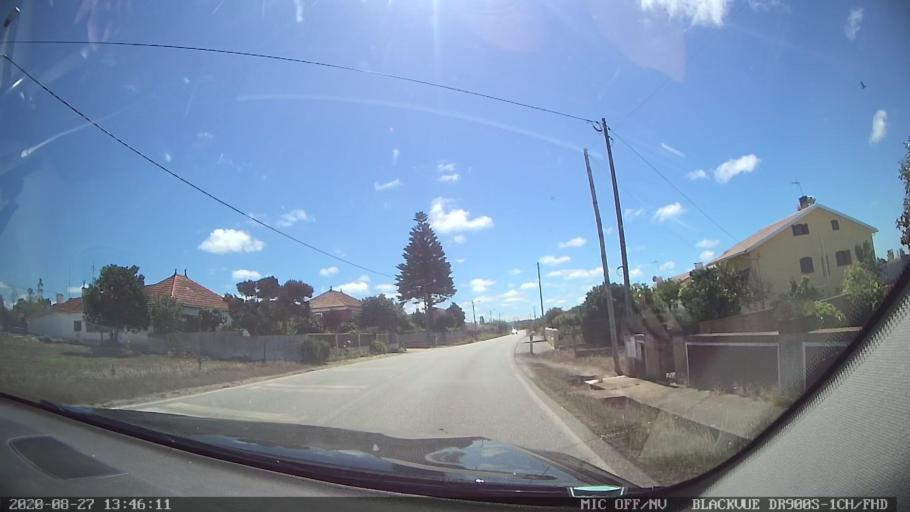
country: PT
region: Coimbra
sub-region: Mira
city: Mira
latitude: 40.3982
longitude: -8.7356
